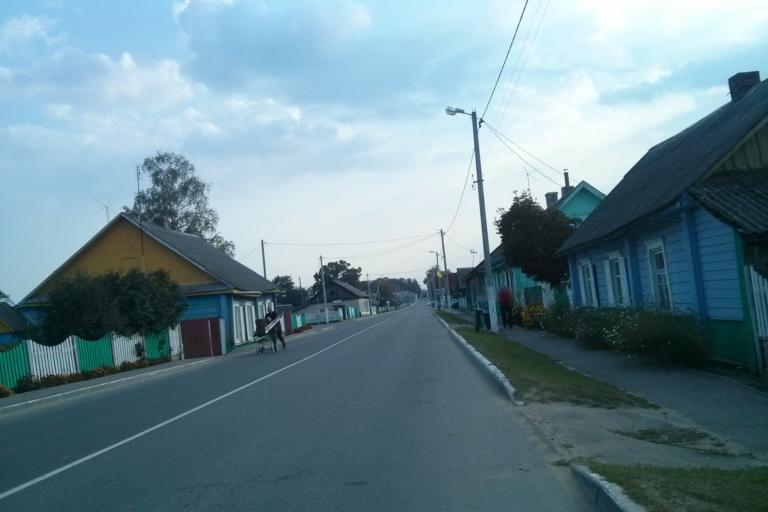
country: BY
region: Minsk
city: Chervyen'
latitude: 53.7198
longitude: 28.4187
